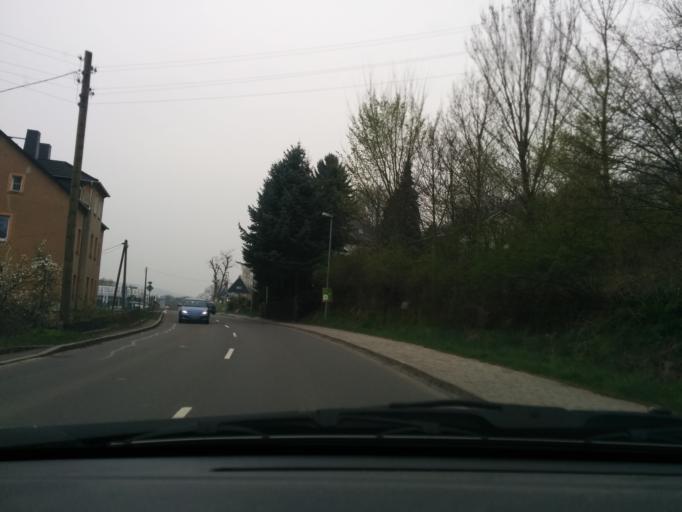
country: DE
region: Saxony
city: Floha
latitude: 50.8618
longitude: 13.0869
